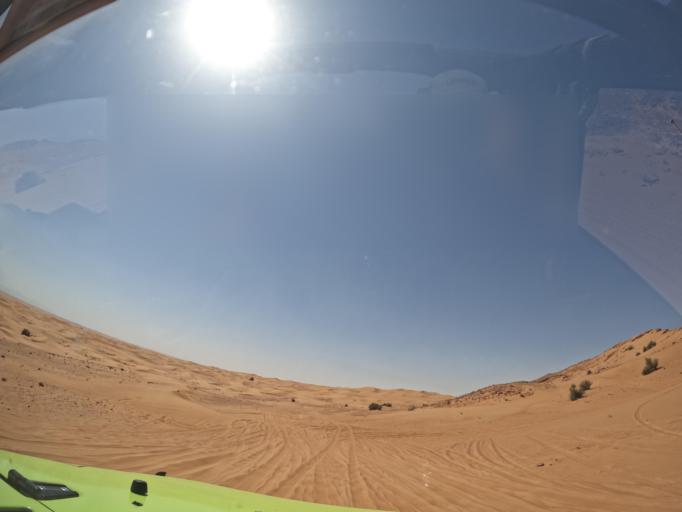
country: AE
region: Ash Shariqah
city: Adh Dhayd
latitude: 25.0201
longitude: 55.7300
